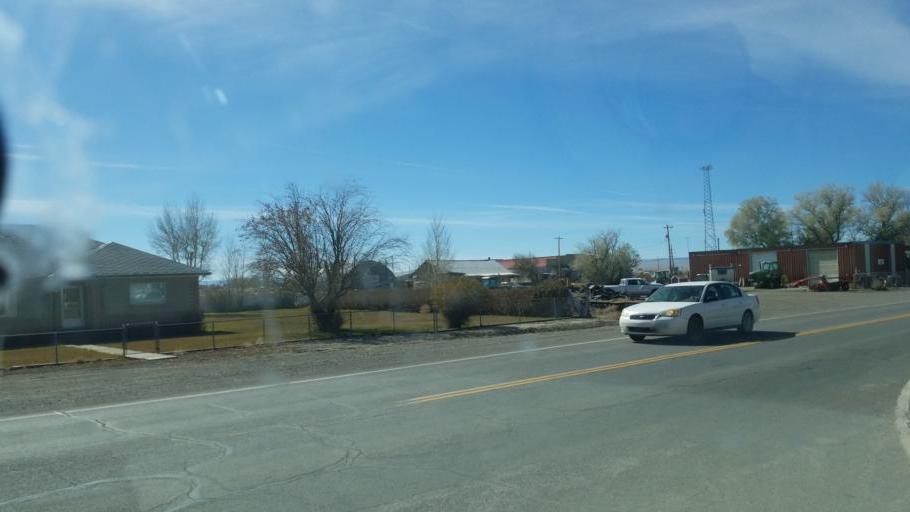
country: US
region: Colorado
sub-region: Conejos County
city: Conejos
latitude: 37.2690
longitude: -105.9607
